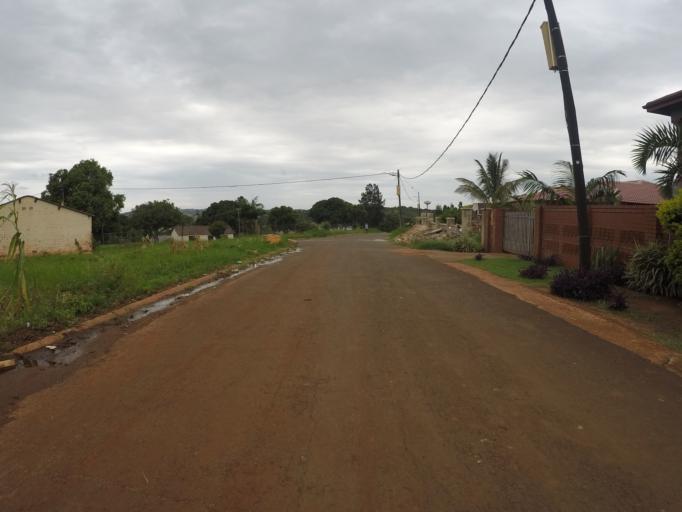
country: ZA
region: KwaZulu-Natal
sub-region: uThungulu District Municipality
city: Empangeni
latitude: -28.7693
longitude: 31.8695
